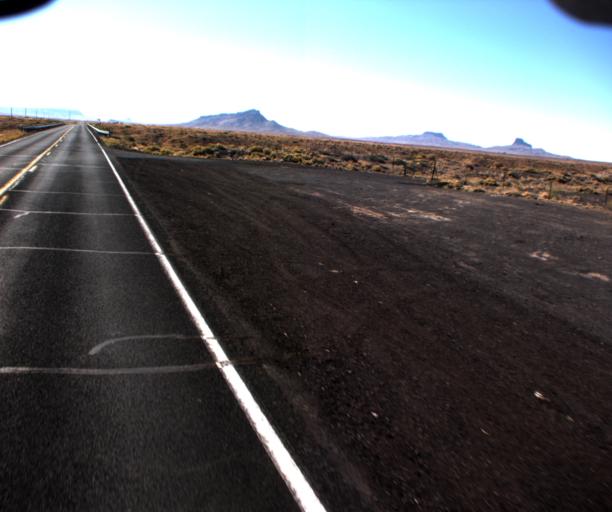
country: US
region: Arizona
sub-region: Navajo County
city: Dilkon
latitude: 35.5524
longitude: -110.4535
